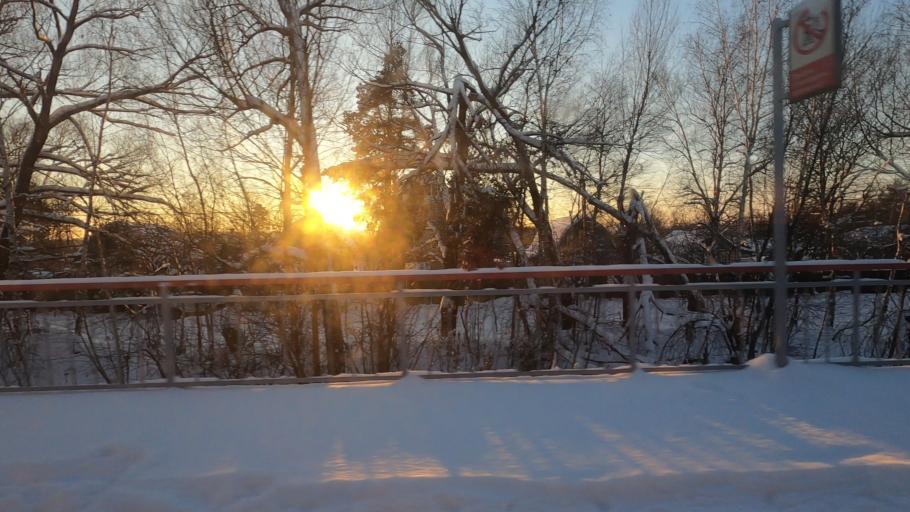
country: RU
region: Moskovskaya
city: Dmitrov
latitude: 56.3820
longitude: 37.5171
